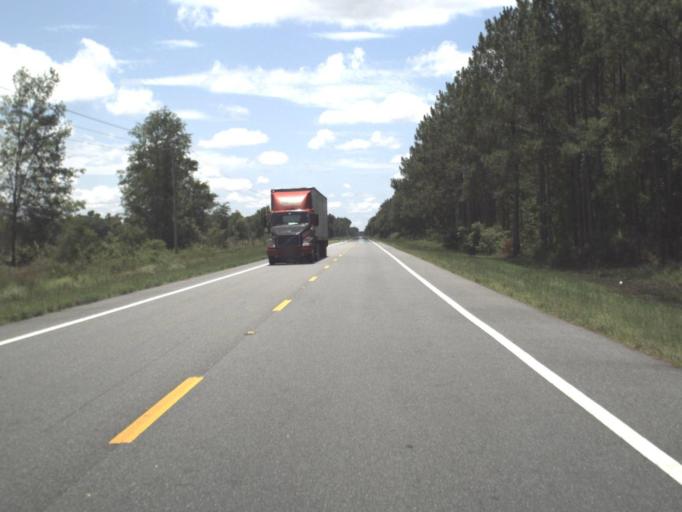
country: US
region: Florida
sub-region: Lafayette County
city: Mayo
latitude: 29.9176
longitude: -82.9513
